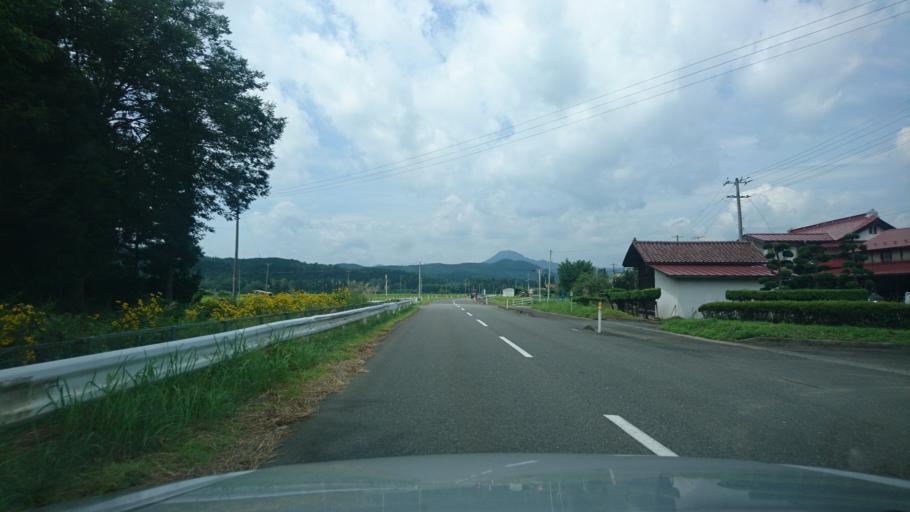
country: JP
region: Iwate
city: Ichinoseki
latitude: 38.8128
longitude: 140.9464
